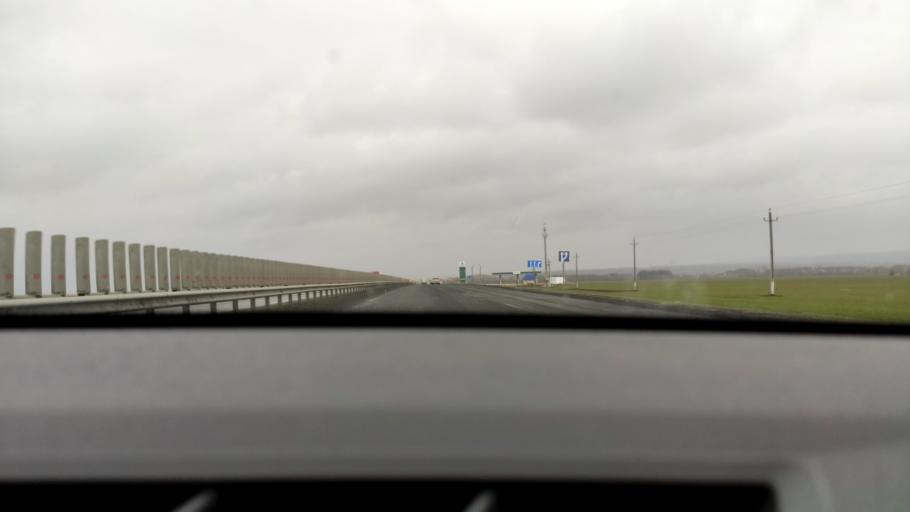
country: RU
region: Samara
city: Bereza
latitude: 53.4661
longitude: 50.1766
